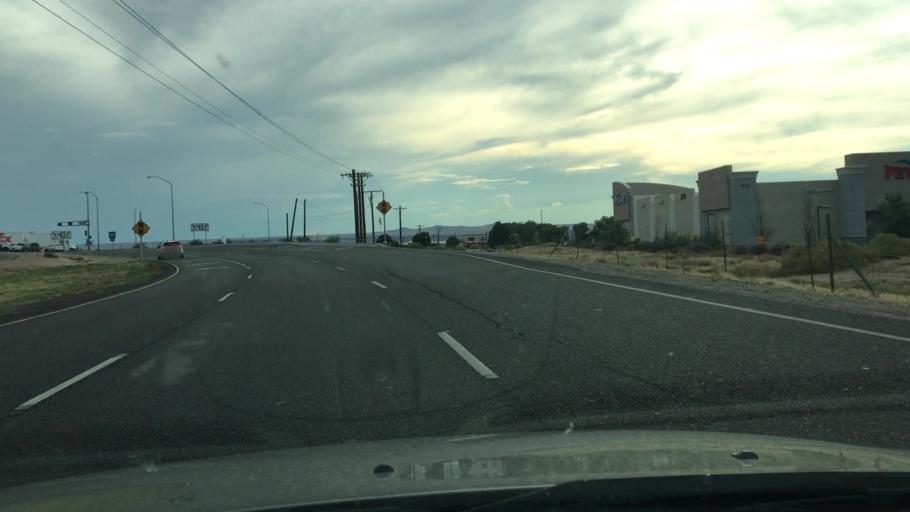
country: US
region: New Mexico
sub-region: Bernalillo County
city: Lee Acres
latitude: 35.1341
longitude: -106.6090
